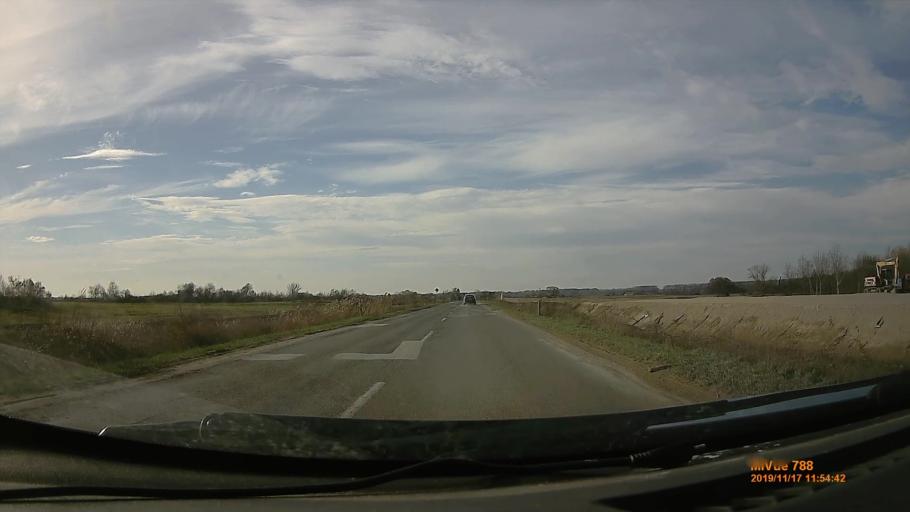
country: HU
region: Bacs-Kiskun
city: Tiszakecske
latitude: 46.8696
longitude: 20.0924
